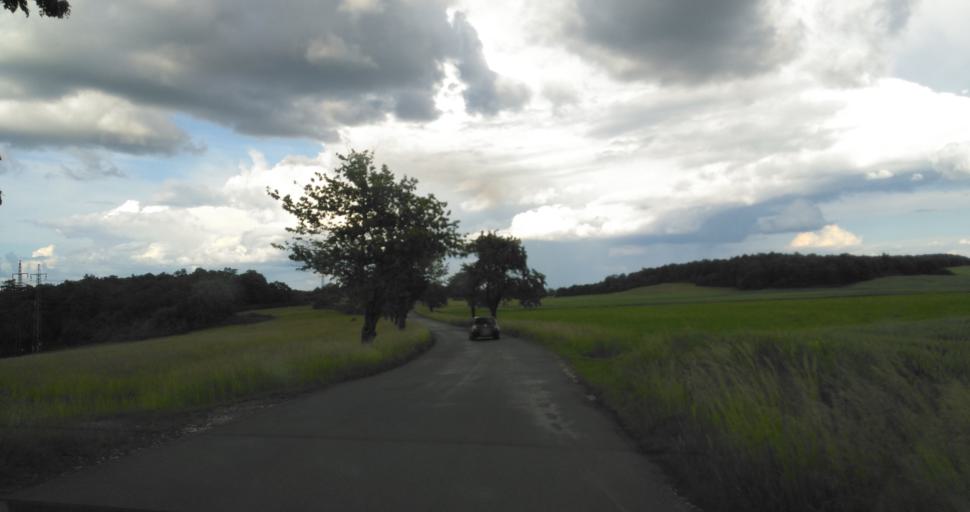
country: CZ
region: Central Bohemia
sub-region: Okres Beroun
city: Beroun
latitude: 49.9238
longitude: 14.1023
